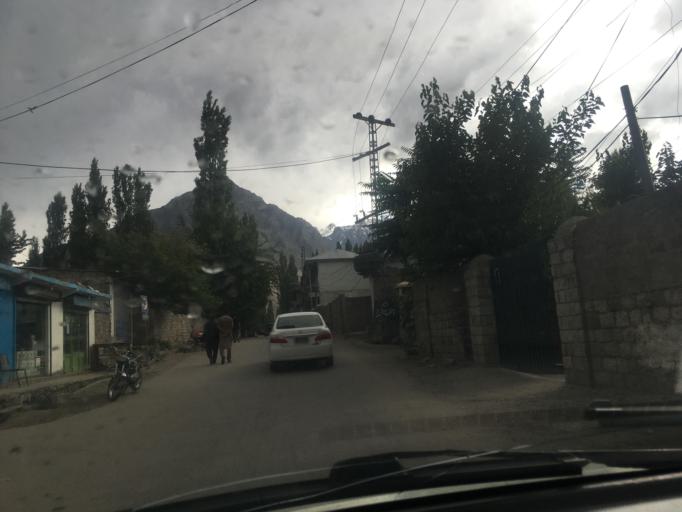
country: PK
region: Gilgit-Baltistan
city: Skardu
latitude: 35.2936
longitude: 75.6493
